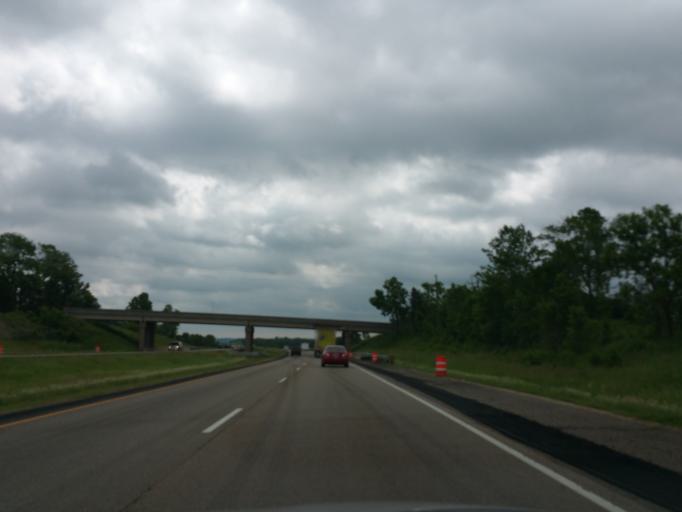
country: US
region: Wisconsin
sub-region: Saint Croix County
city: Woodville
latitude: 44.9360
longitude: -92.3205
